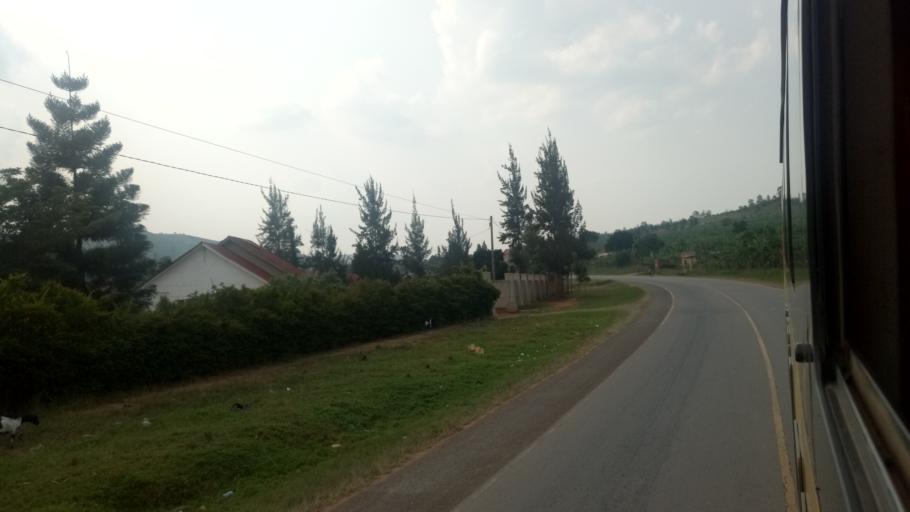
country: UG
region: Western Region
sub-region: Mbarara District
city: Mbarara
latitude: -0.5504
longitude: 30.7139
